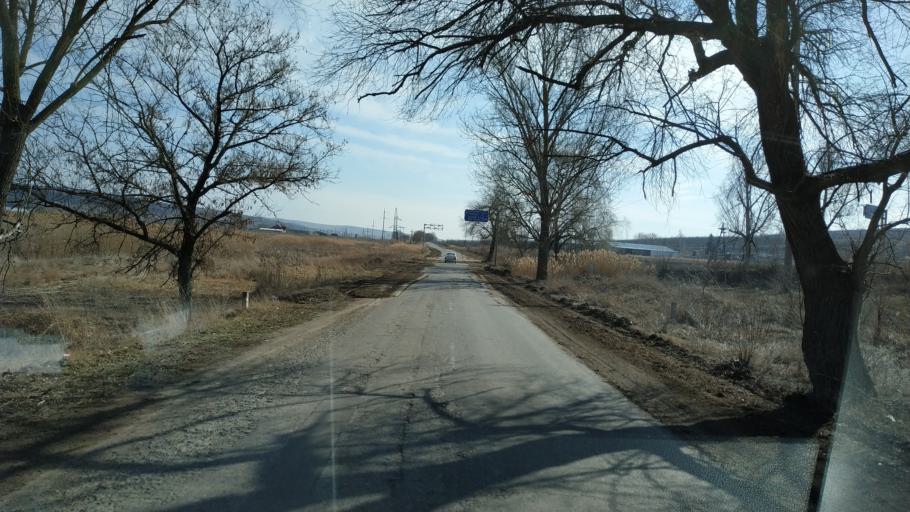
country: MD
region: Nisporeni
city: Nisporeni
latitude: 47.0893
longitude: 28.1378
